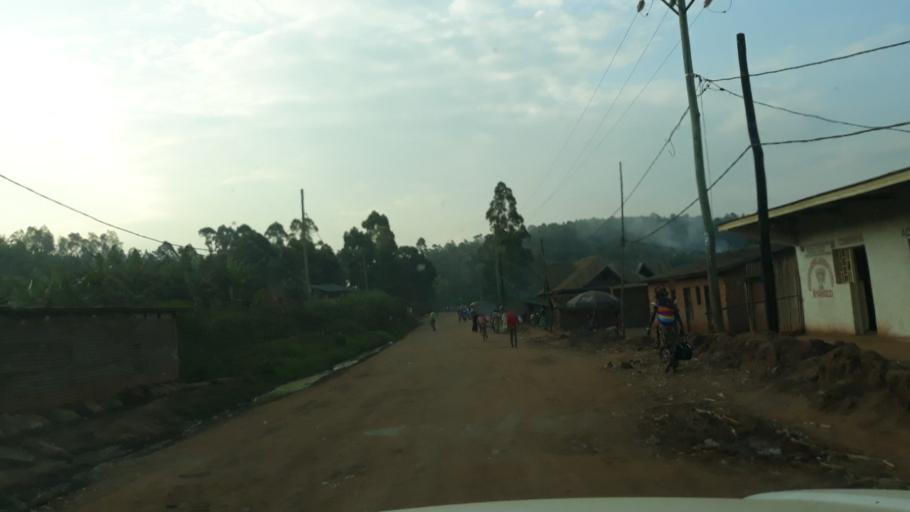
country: CD
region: South Kivu
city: Bukavu
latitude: -2.6580
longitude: 28.8739
